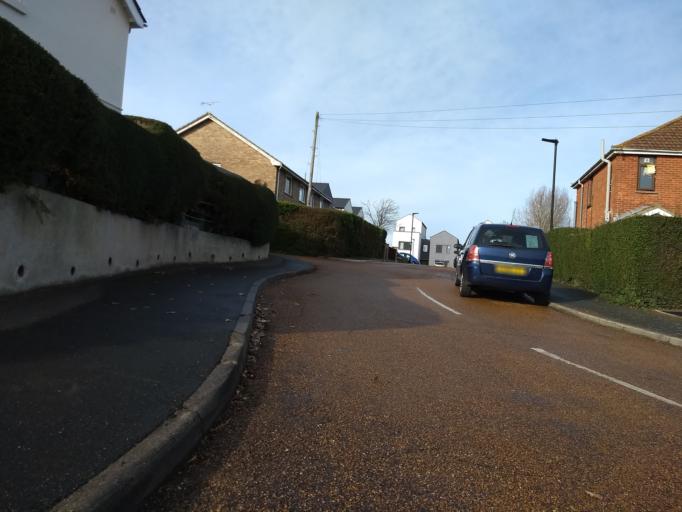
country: GB
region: England
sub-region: Isle of Wight
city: Totland
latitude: 50.6798
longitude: -1.5206
